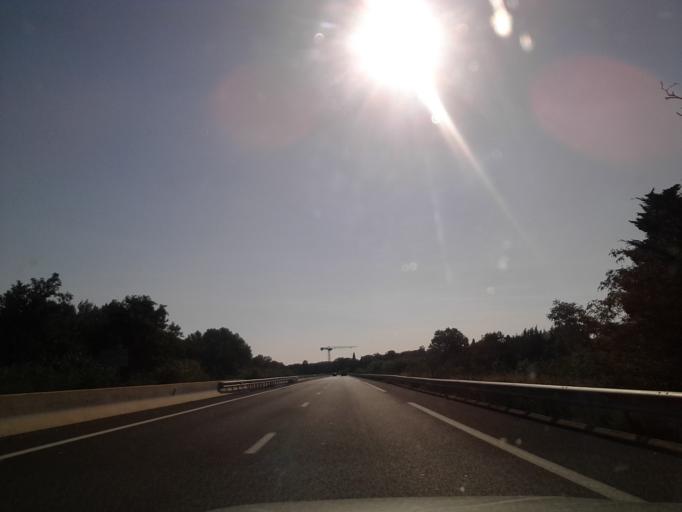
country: FR
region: Languedoc-Roussillon
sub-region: Departement des Pyrenees-Orientales
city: Ille-sur-Tet
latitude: 42.6744
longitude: 2.6166
